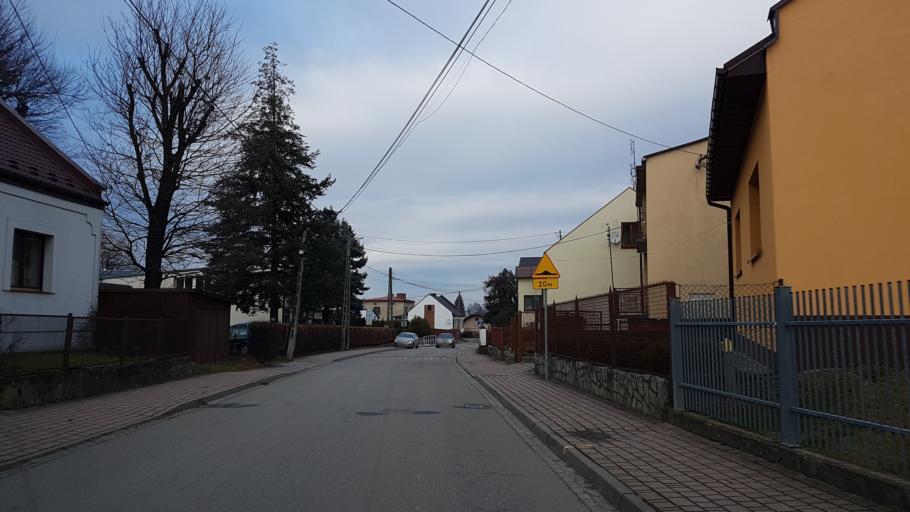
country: PL
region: Lesser Poland Voivodeship
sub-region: Powiat nowosadecki
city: Stary Sacz
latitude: 49.5571
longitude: 20.6335
